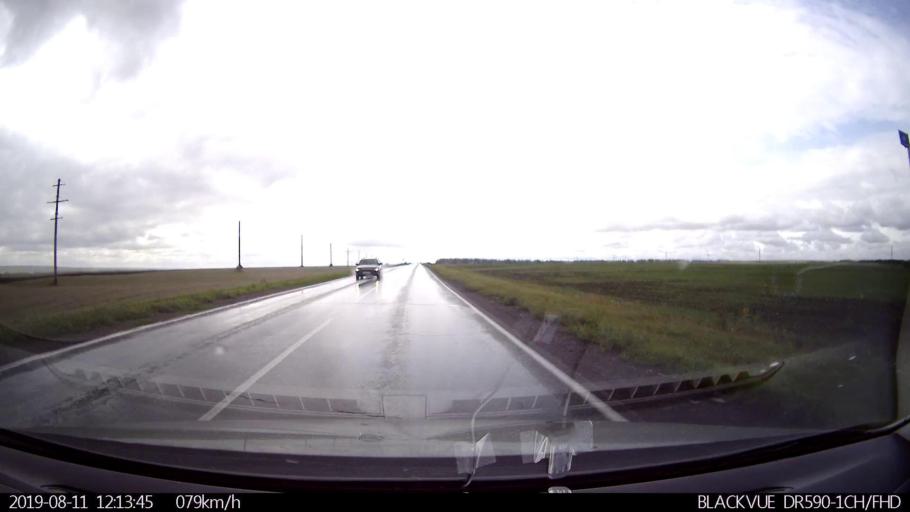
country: RU
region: Ulyanovsk
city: Ignatovka
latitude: 53.9589
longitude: 47.9891
